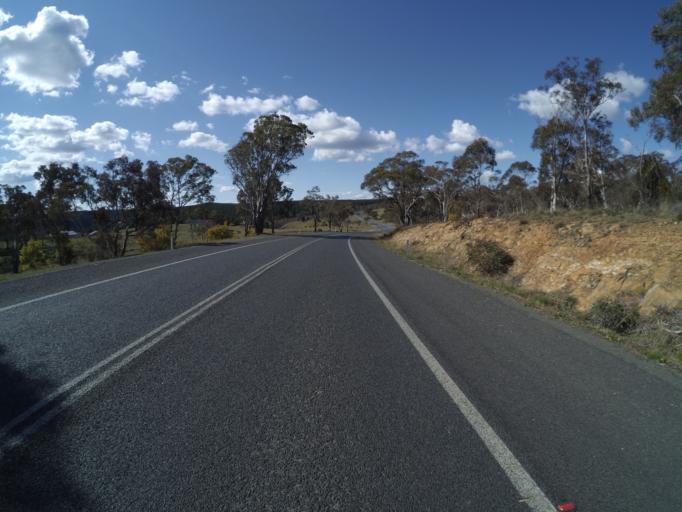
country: AU
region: New South Wales
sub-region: Queanbeyan
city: Queanbeyan
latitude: -35.3414
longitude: 149.2837
